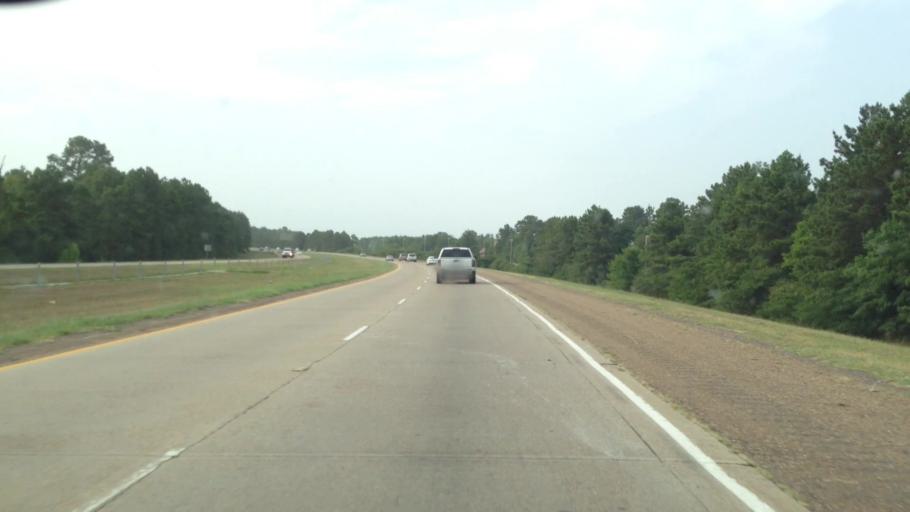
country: US
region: Louisiana
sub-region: Caddo Parish
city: Shreveport
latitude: 32.4285
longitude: -93.8395
